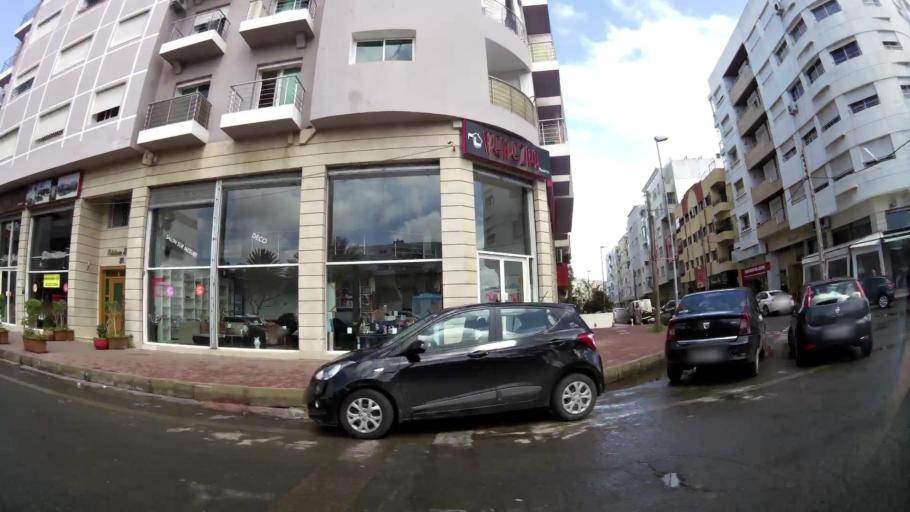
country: MA
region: Grand Casablanca
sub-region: Casablanca
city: Casablanca
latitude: 33.5723
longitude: -7.6373
